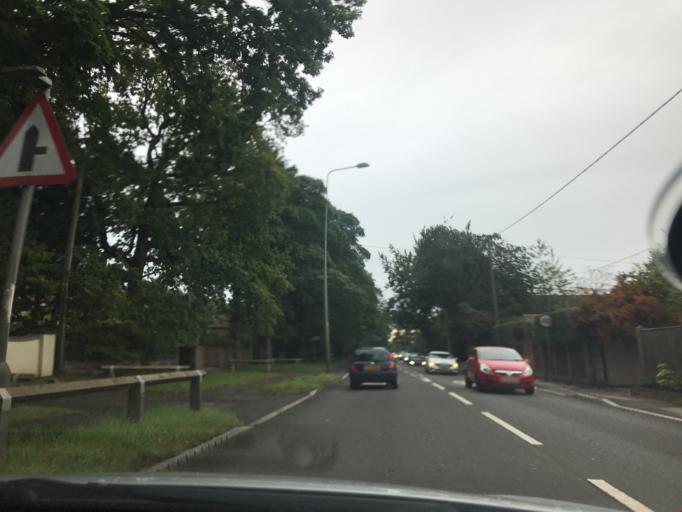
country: GB
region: England
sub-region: Cheshire West and Chester
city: Cuddington
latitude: 53.2304
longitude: -2.5986
